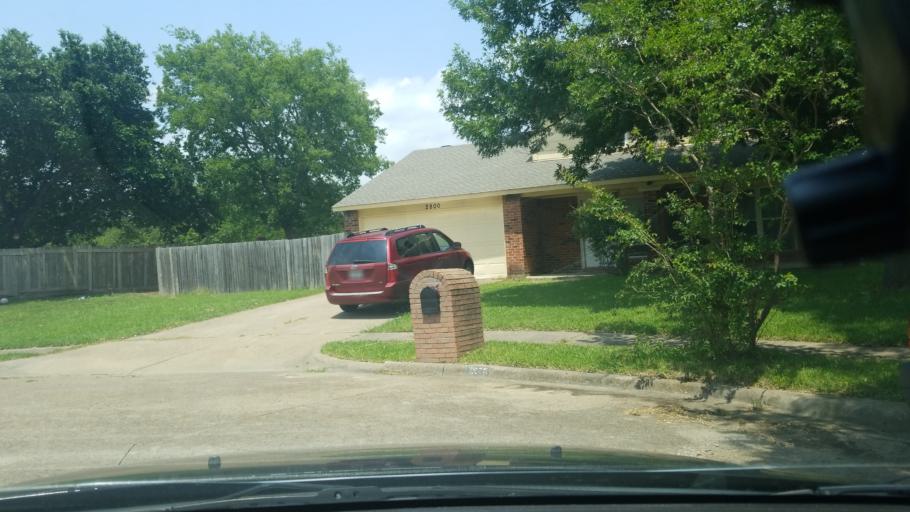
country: US
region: Texas
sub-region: Dallas County
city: Mesquite
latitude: 32.8087
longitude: -96.6415
